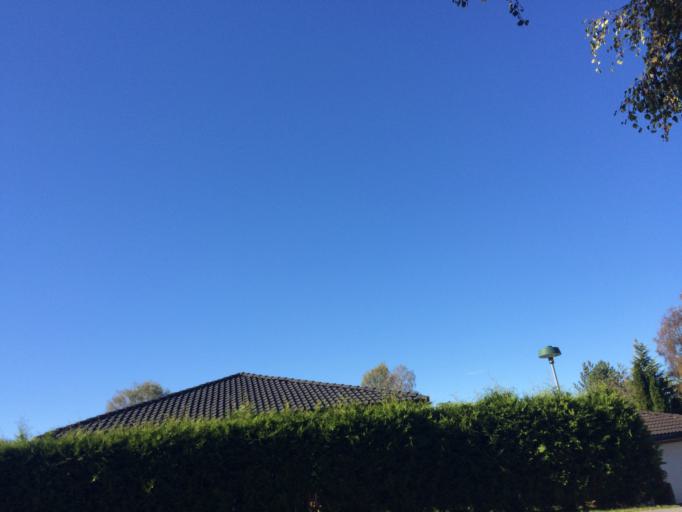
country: NO
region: Akershus
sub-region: Ski
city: Ski
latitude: 59.7188
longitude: 10.8060
